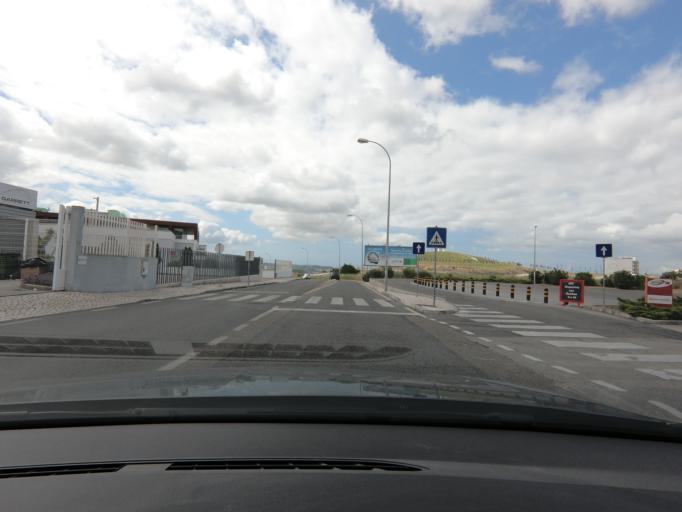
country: PT
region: Lisbon
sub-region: Oeiras
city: Carnaxide
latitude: 38.7311
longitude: -9.2256
